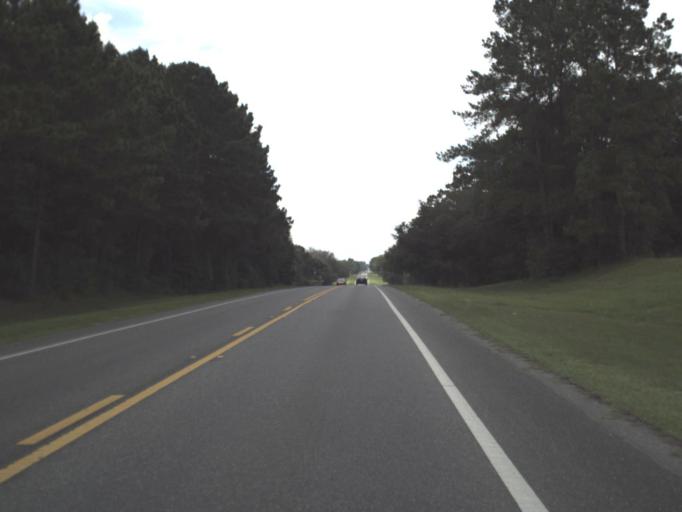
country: US
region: Florida
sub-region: Suwannee County
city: Live Oak
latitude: 30.2383
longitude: -82.9880
